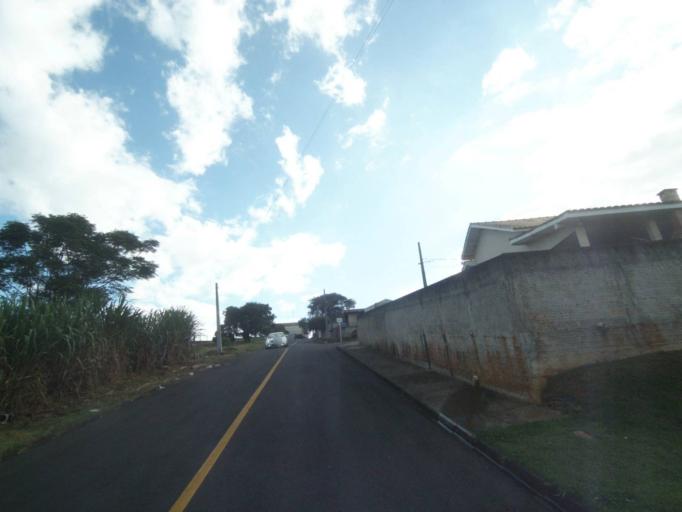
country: BR
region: Parana
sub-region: Telemaco Borba
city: Telemaco Borba
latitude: -24.3405
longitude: -50.6180
